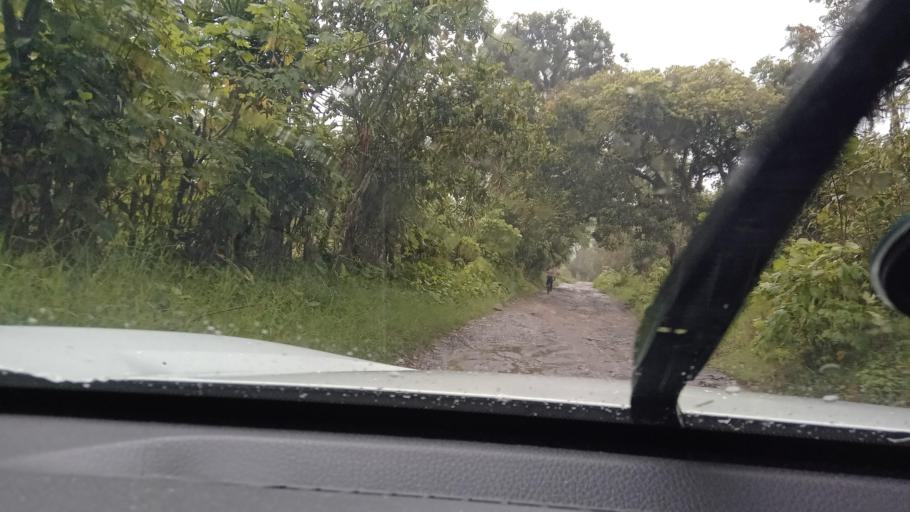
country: MX
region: Veracruz
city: Coatepec
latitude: 19.4559
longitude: -96.9767
